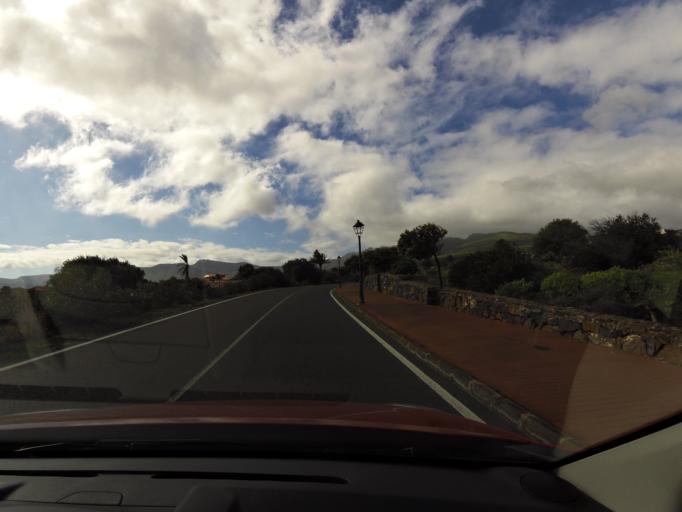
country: ES
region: Canary Islands
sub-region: Provincia de Las Palmas
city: Aguimes
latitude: 27.9036
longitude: -15.4513
